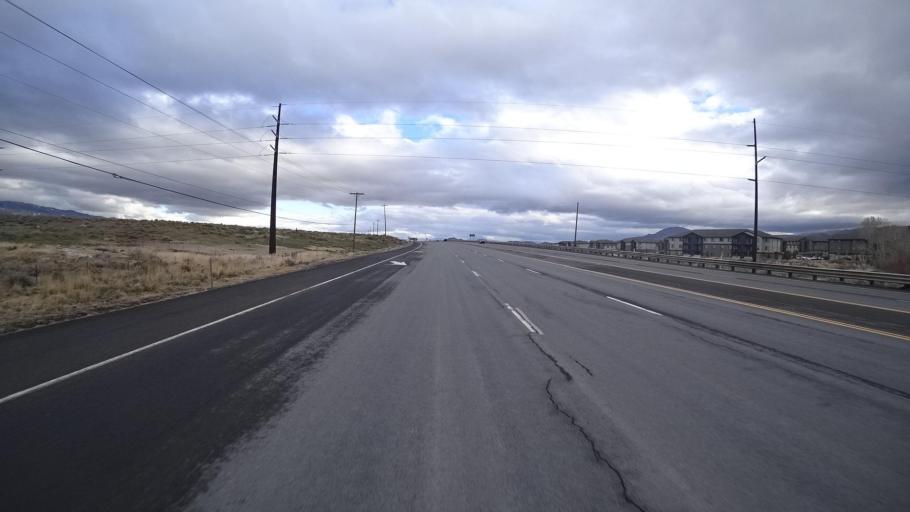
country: US
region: Nevada
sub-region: Storey County
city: Virginia City
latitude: 39.3966
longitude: -119.7431
